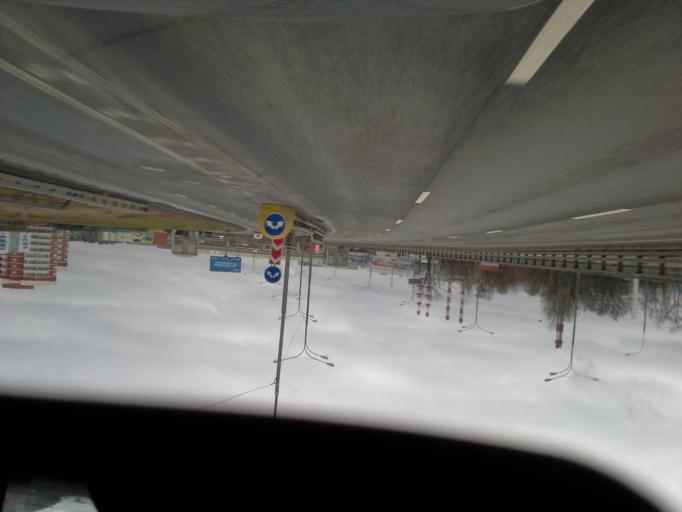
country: RU
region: Moskovskaya
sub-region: Leninskiy Rayon
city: Vnukovo
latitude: 55.6168
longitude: 37.2662
